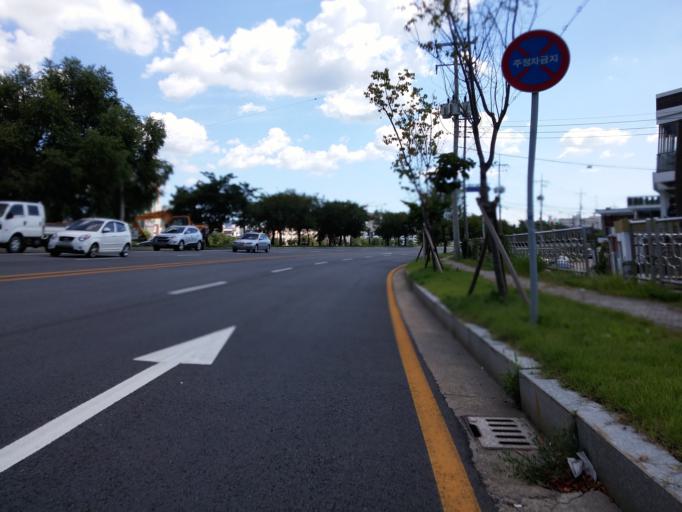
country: KR
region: Chungcheongbuk-do
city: Cheongju-si
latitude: 36.6226
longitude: 127.4920
